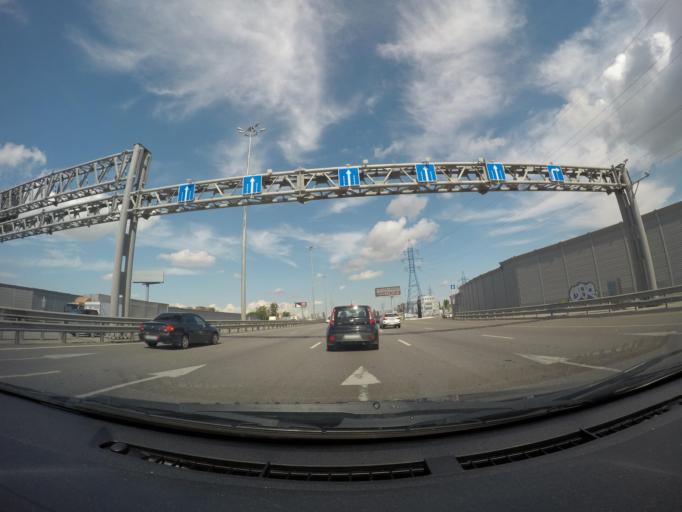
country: RU
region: Moskovskaya
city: Lyubertsy
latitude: 55.6568
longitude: 37.8980
